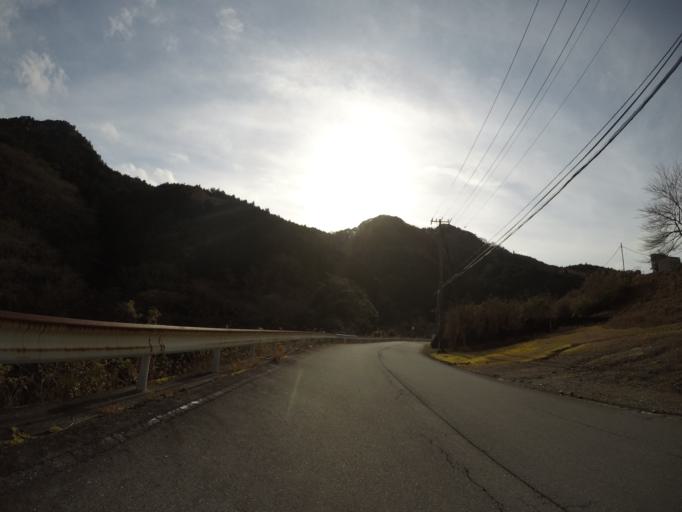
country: JP
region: Shizuoka
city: Heda
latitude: 34.8888
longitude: 138.8689
